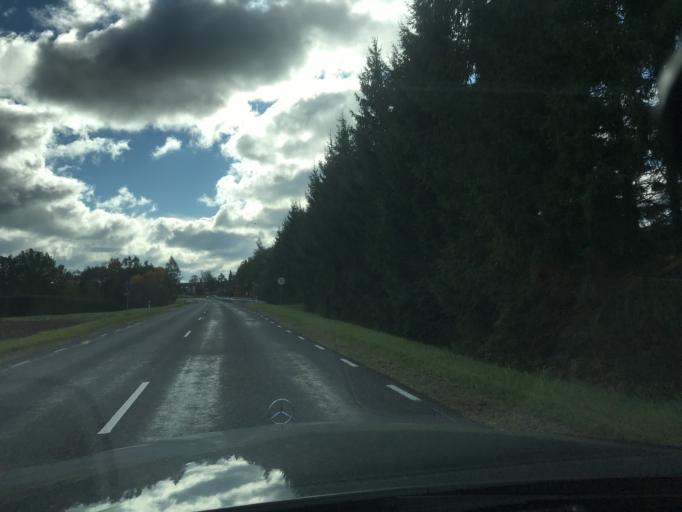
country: EE
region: Vorumaa
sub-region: Antsla vald
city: Vana-Antsla
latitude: 57.9583
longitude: 26.2744
